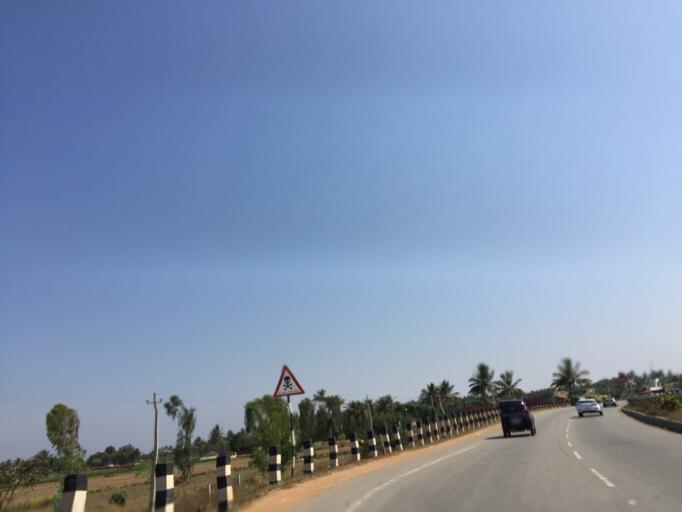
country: IN
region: Karnataka
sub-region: Bangalore Rural
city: Dasarahalli
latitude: 13.0870
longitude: 77.8269
